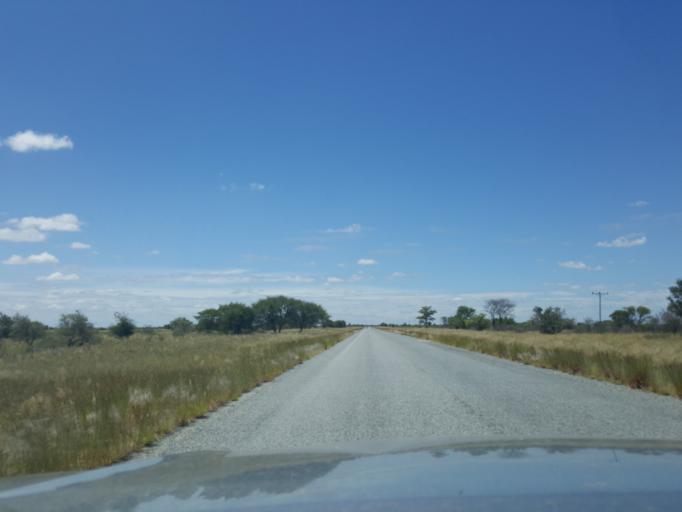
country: BW
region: Central
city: Nata
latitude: -20.1991
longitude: 26.1112
